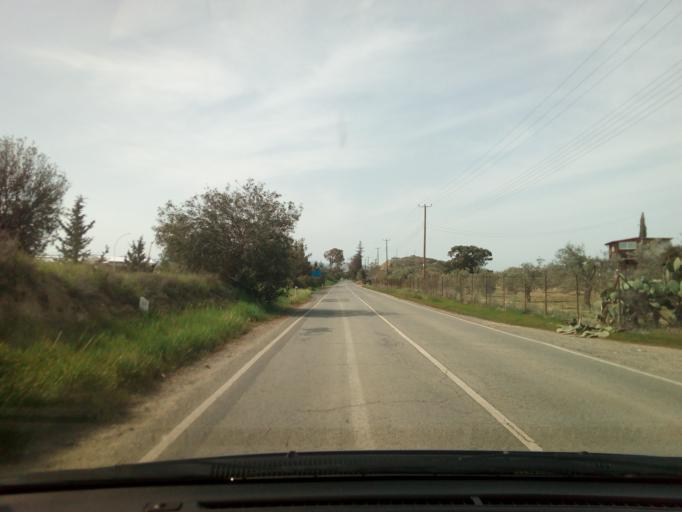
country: CY
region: Lefkosia
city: Ergates
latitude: 35.0701
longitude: 33.2333
